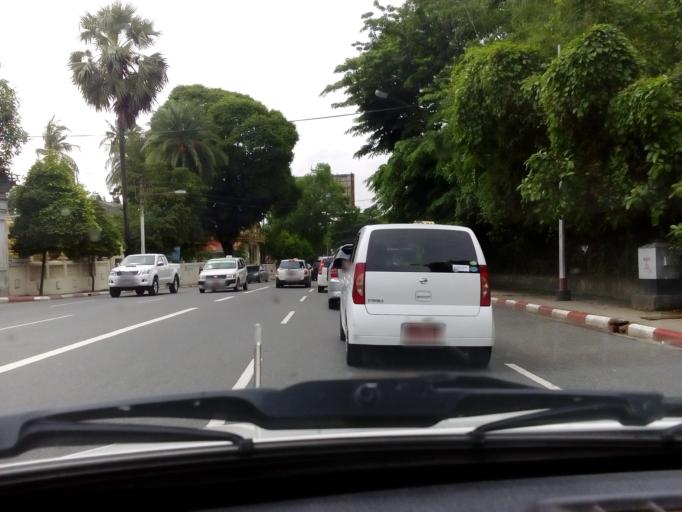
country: MM
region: Yangon
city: Yangon
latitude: 16.8221
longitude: 96.1544
